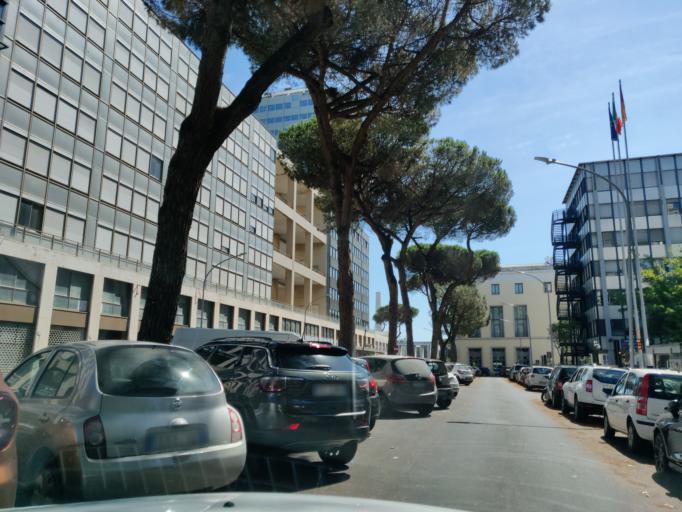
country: IT
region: Latium
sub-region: Citta metropolitana di Roma Capitale
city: Selcetta
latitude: 41.8340
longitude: 12.4679
